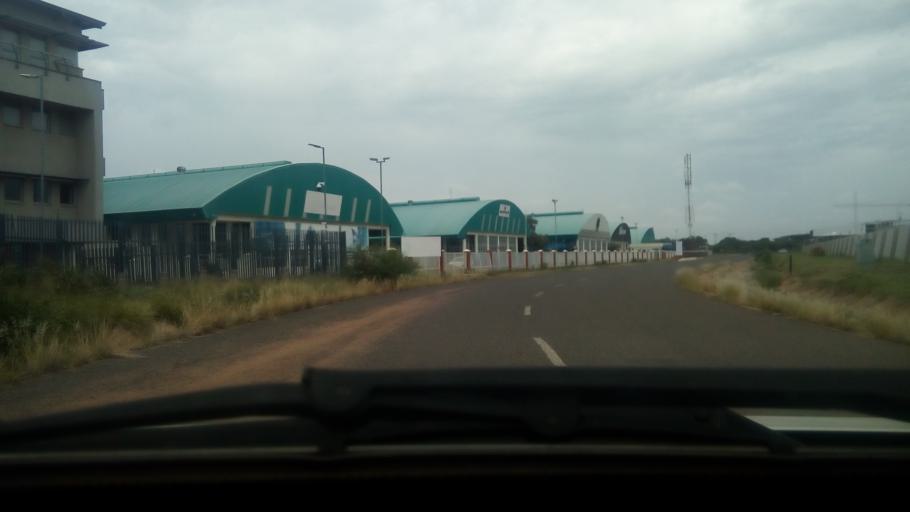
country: BW
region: Kweneng
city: Mmopone
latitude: -24.5884
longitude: 25.9147
